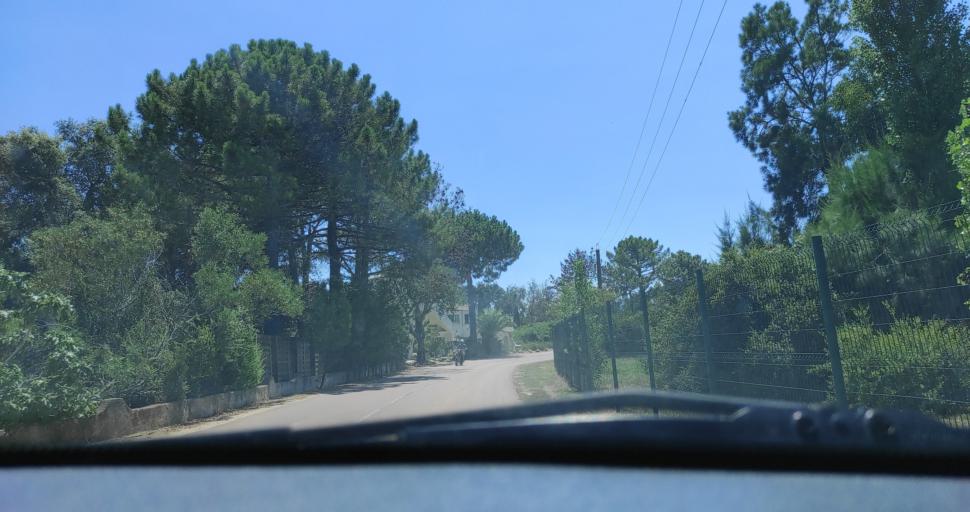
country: FR
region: Corsica
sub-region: Departement de la Corse-du-Sud
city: Porto-Vecchio
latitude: 41.6259
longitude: 9.3367
